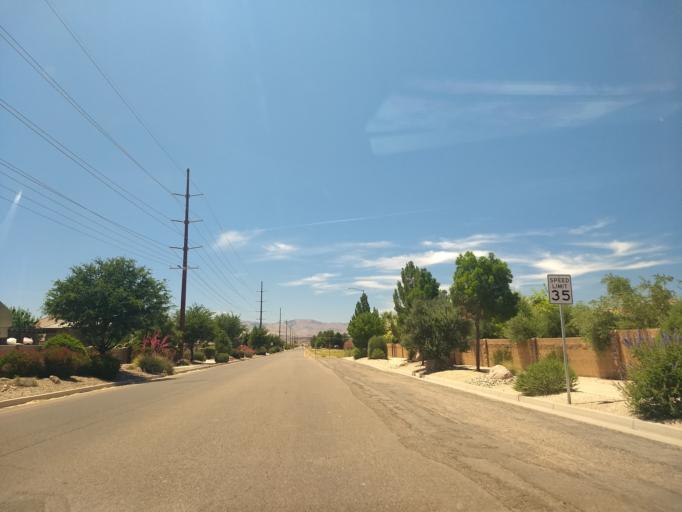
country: US
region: Utah
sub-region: Washington County
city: Washington
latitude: 37.0889
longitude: -113.5056
